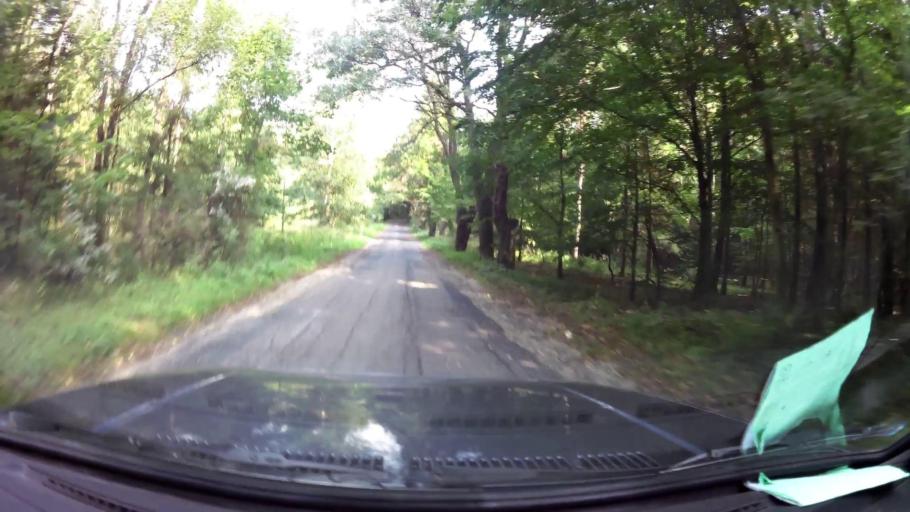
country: PL
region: West Pomeranian Voivodeship
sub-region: Powiat koszalinski
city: Polanow
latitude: 54.1320
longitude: 16.5215
